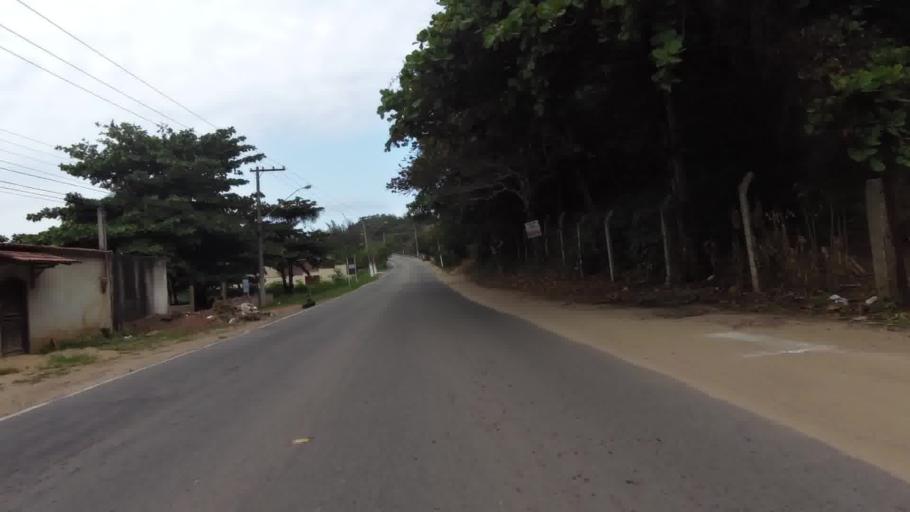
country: BR
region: Espirito Santo
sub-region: Piuma
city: Piuma
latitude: -20.8637
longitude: -40.7596
